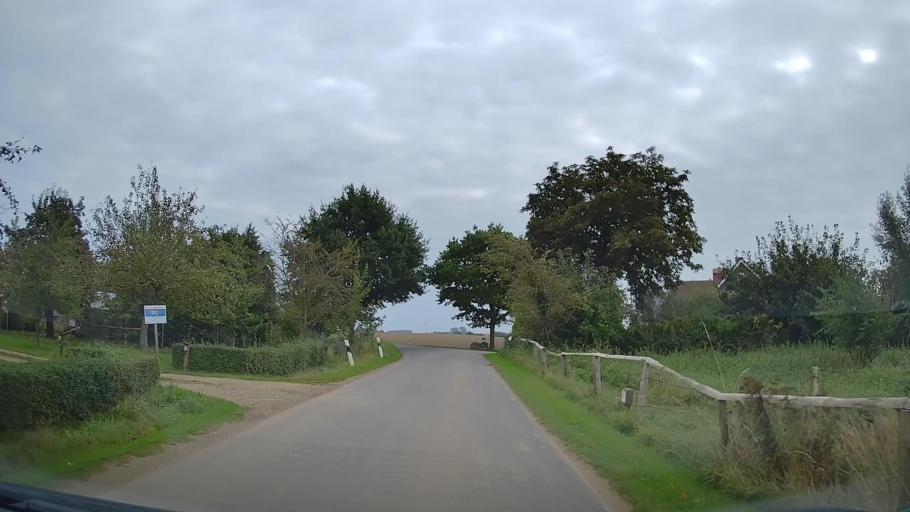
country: DE
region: Schleswig-Holstein
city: Hohenfelde
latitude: 54.3742
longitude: 10.5235
